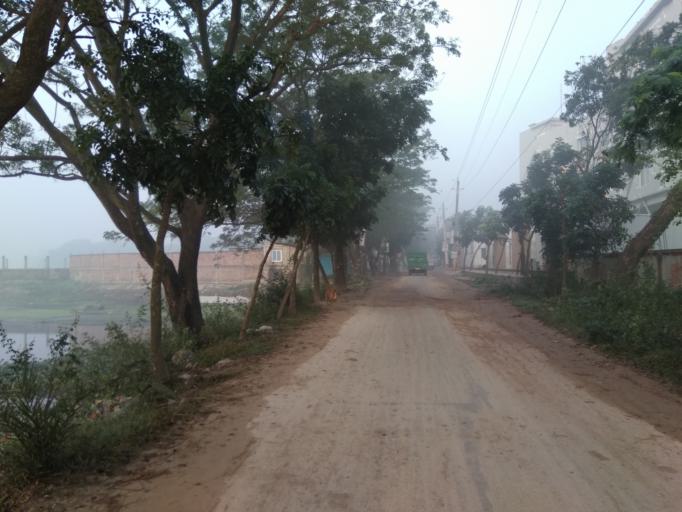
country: BD
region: Dhaka
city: Tungi
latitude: 23.8618
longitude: 90.4471
